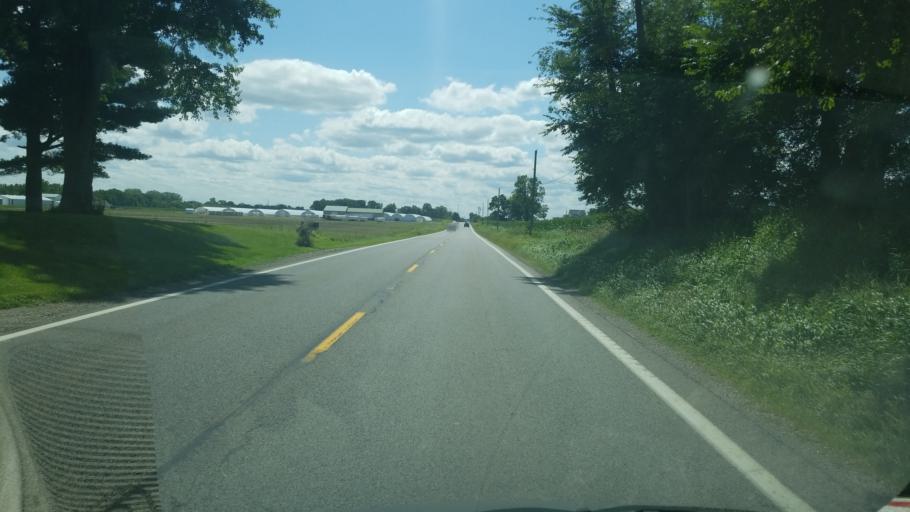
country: US
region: Ohio
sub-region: Fulton County
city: Delta
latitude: 41.6105
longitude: -84.0375
